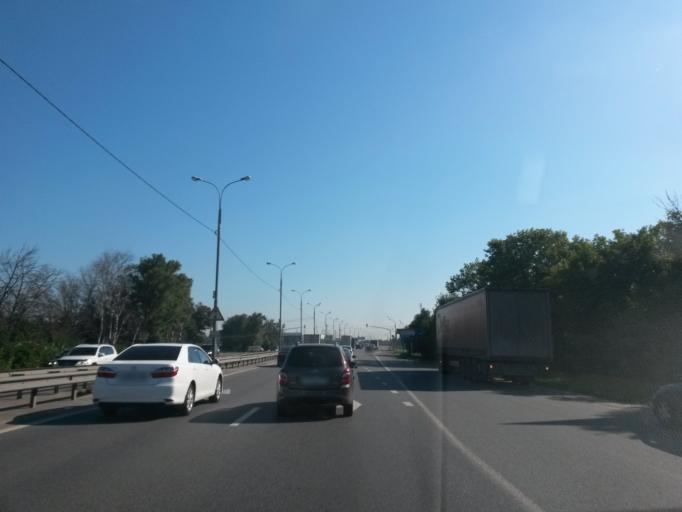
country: RU
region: Moskovskaya
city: Lesnyye Polyany
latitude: 55.9782
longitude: 37.8600
